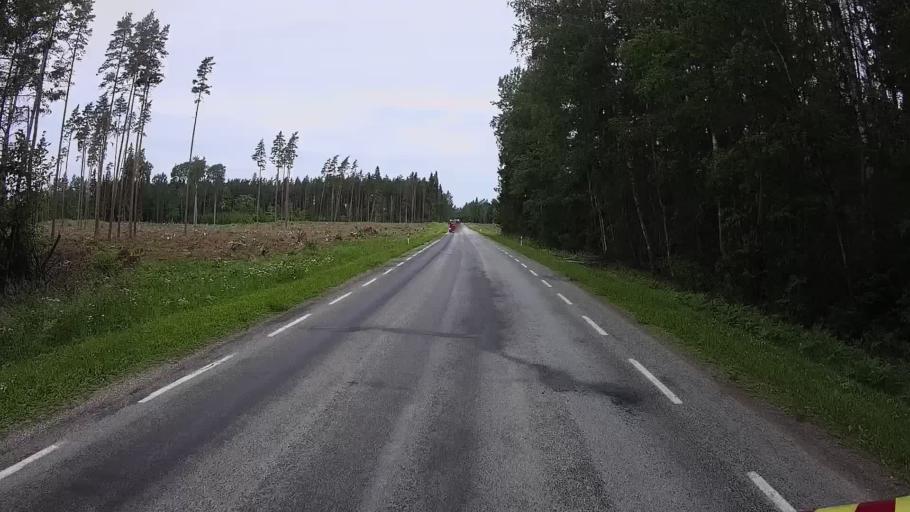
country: EE
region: Viljandimaa
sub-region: Karksi vald
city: Karksi-Nuia
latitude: 58.2186
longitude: 25.6185
